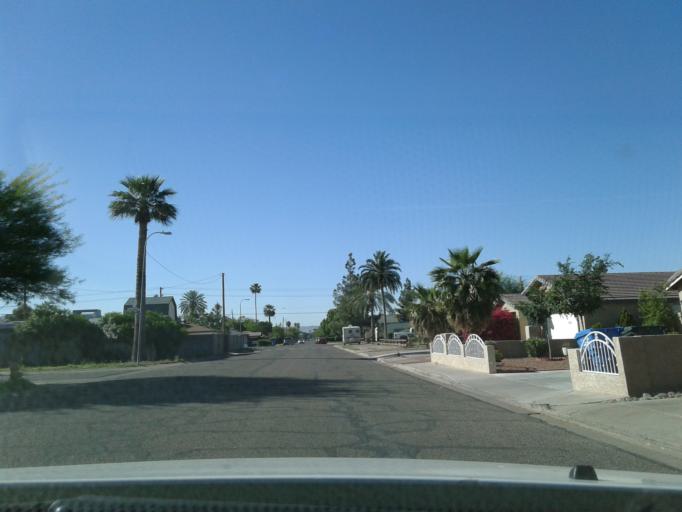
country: US
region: Arizona
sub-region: Maricopa County
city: Phoenix
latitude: 33.5142
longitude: -112.1041
